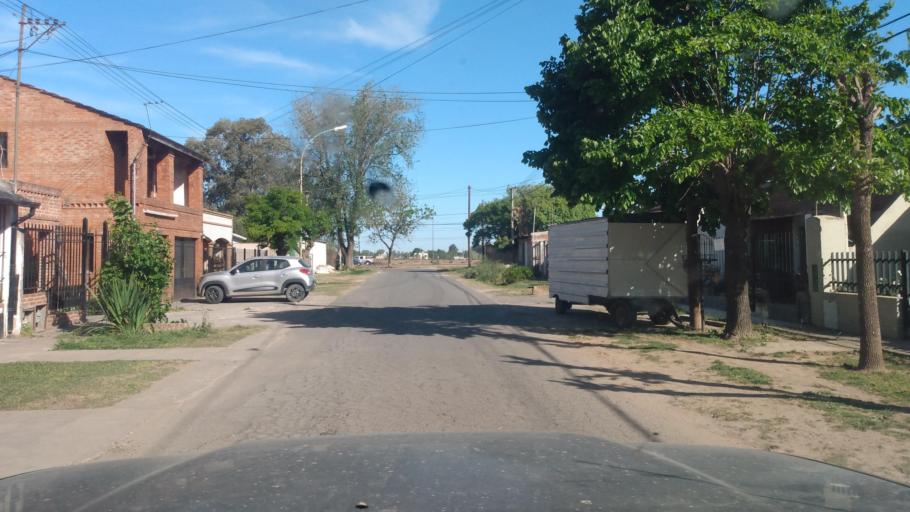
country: AR
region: Buenos Aires
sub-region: Partido de Lujan
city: Lujan
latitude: -34.5630
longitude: -59.1416
